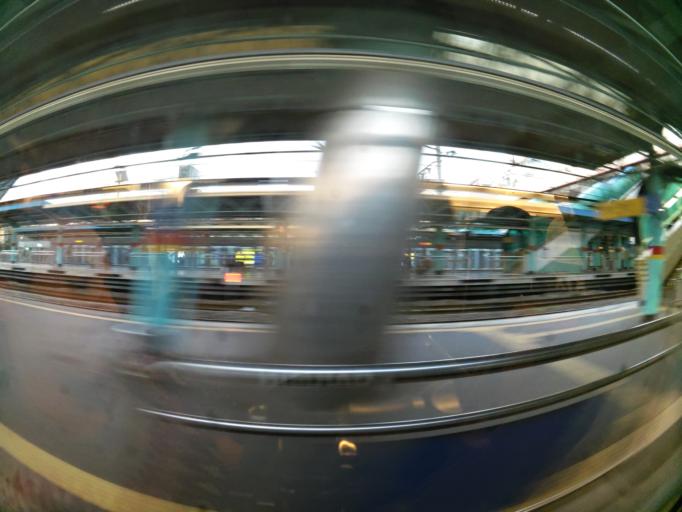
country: KR
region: Gyeonggi-do
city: Kwangmyong
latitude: 37.5150
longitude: 126.9064
